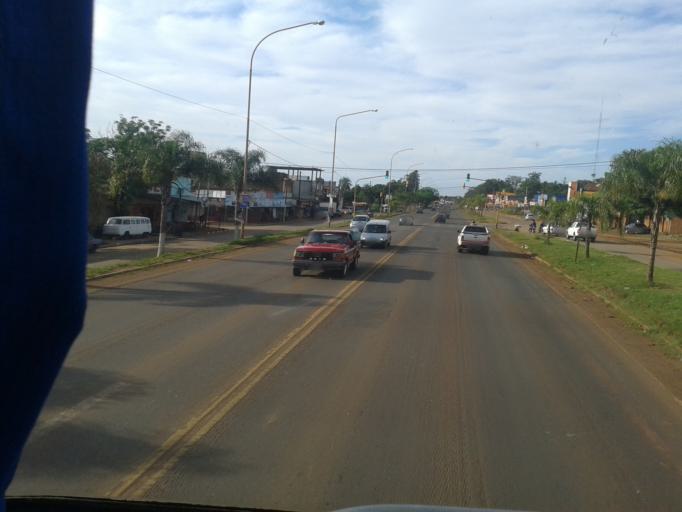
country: AR
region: Misiones
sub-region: Departamento de Capital
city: Posadas
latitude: -27.4099
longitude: -55.9022
